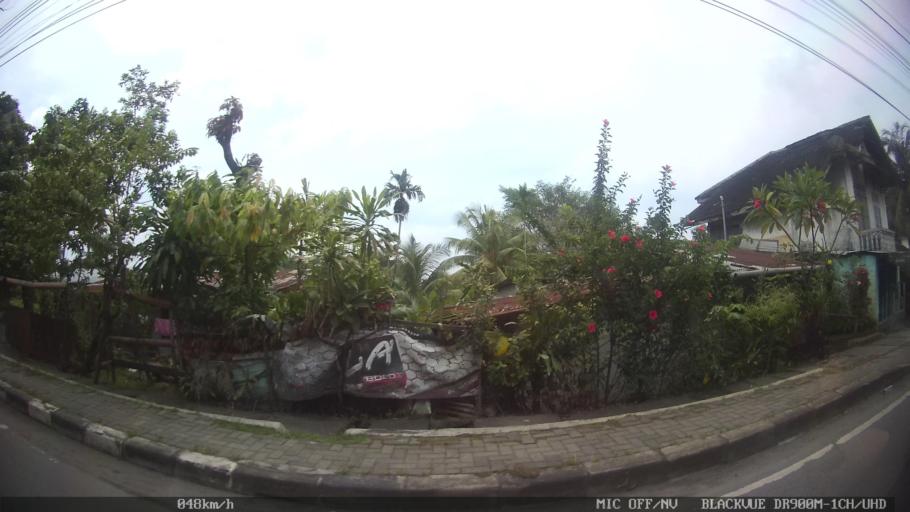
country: ID
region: North Sumatra
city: Medan
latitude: 3.6298
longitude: 98.6718
